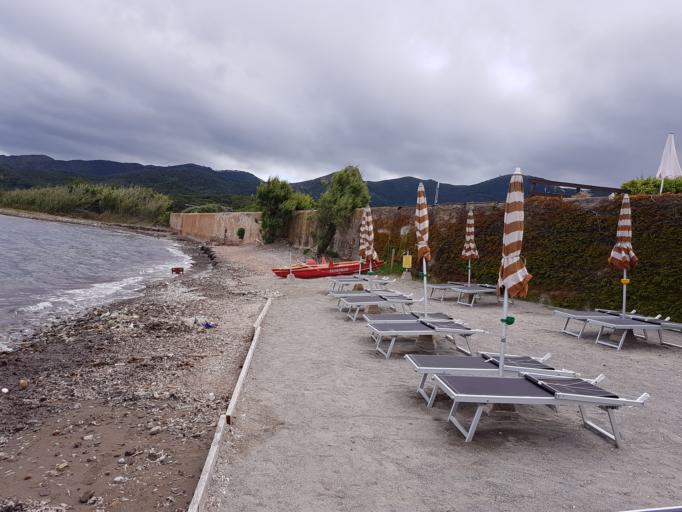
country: IT
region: Tuscany
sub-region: Provincia di Livorno
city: Portoferraio
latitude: 42.7977
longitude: 10.3519
